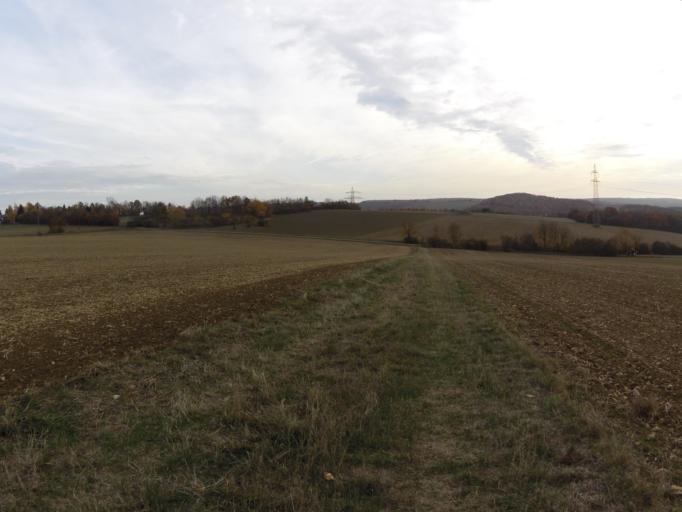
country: DE
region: Bavaria
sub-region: Regierungsbezirk Unterfranken
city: Eisingen
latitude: 49.7557
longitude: 9.8268
